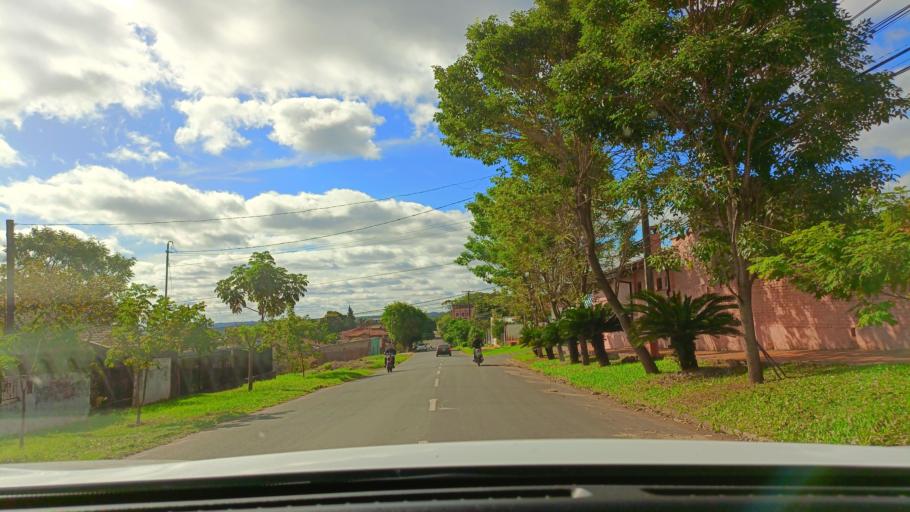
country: PY
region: San Pedro
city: Guayaybi
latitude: -24.6690
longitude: -56.4461
